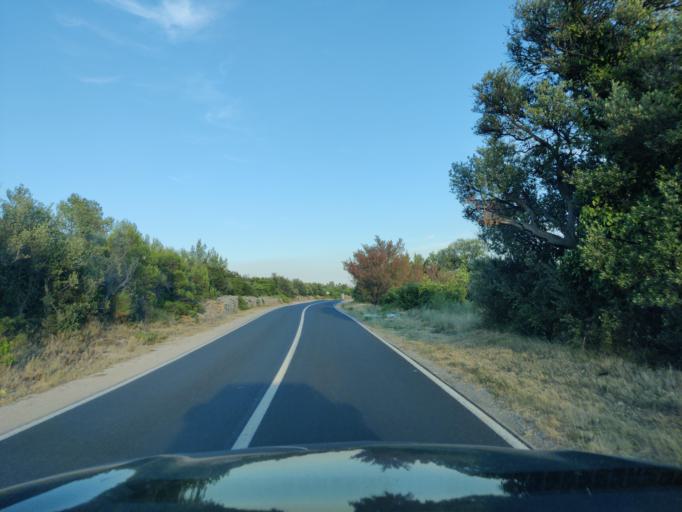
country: HR
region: Sibensko-Kniniska
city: Tribunj
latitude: 43.7662
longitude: 15.7343
